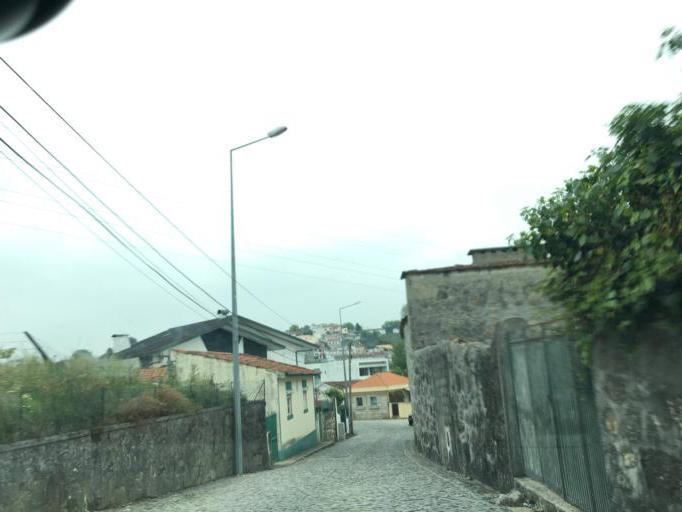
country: PT
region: Porto
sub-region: Maia
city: Nogueira
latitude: 41.2429
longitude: -8.6009
